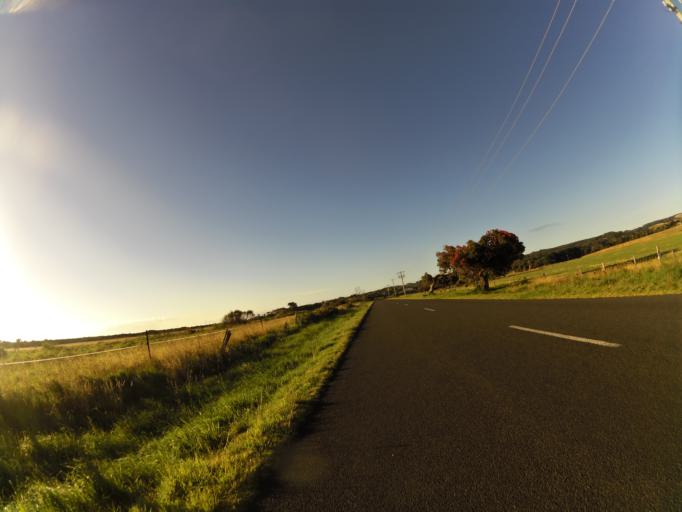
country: AU
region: Victoria
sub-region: Colac-Otway
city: Apollo Bay
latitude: -38.7635
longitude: 143.6616
